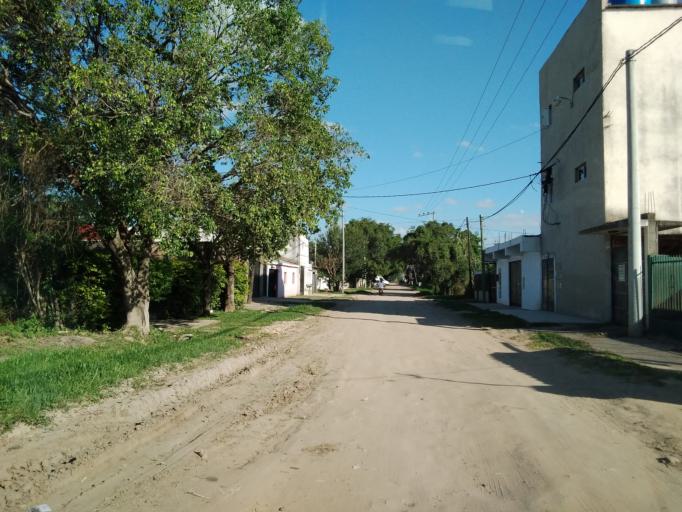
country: AR
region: Corrientes
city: Corrientes
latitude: -27.4615
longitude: -58.7788
